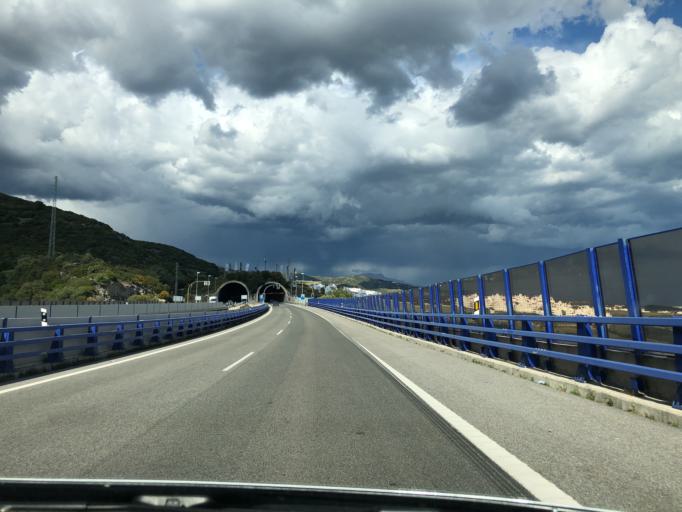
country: ES
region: Andalusia
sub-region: Provincia de Malaga
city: Estepona
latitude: 36.4264
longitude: -5.2050
